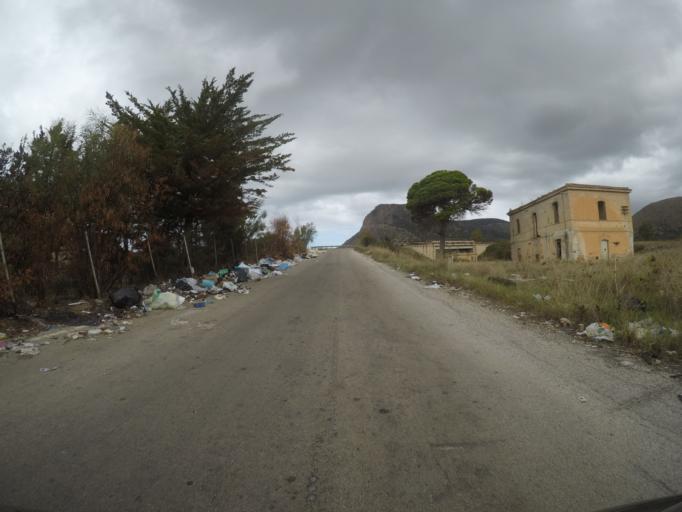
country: IT
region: Sicily
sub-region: Palermo
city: Partinico
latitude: 38.0829
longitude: 13.1087
